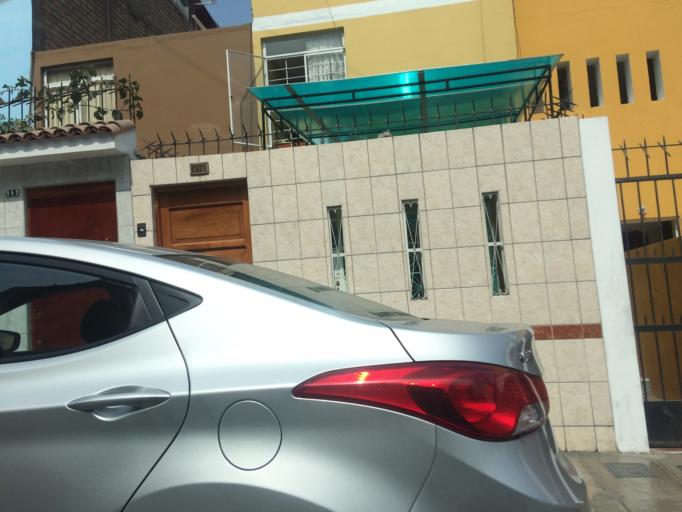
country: PE
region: Lima
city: Lima
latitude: -12.0303
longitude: -77.0366
